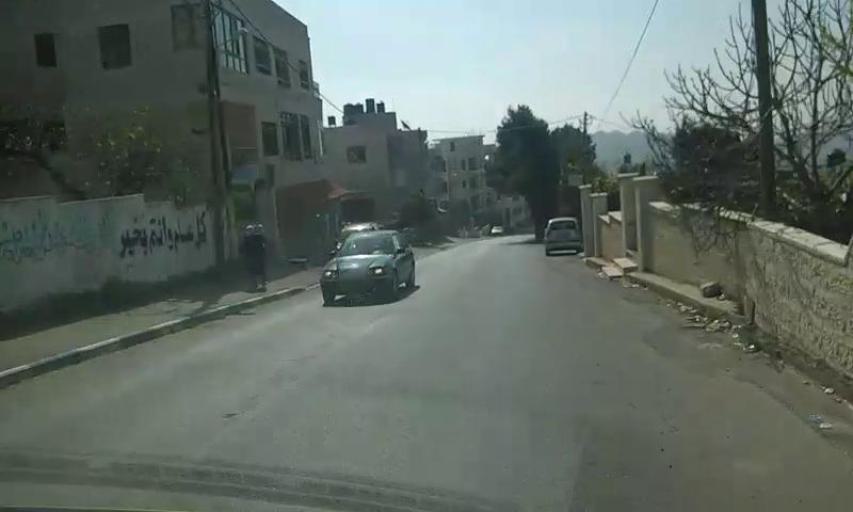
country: PS
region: West Bank
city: Dayr Jarir
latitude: 31.9648
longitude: 35.2934
